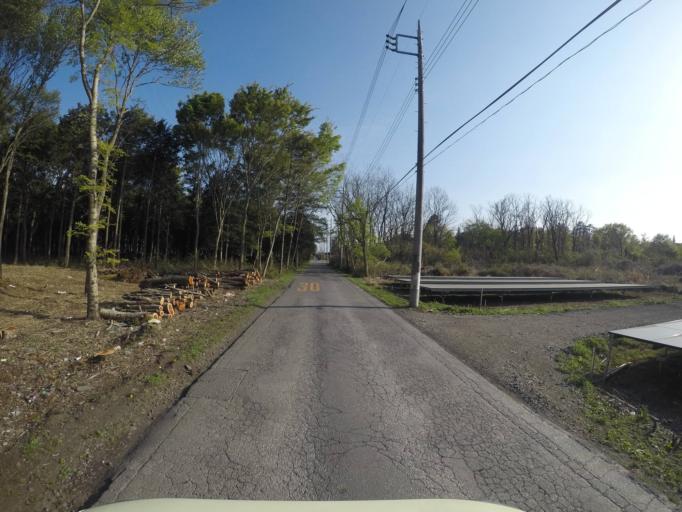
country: JP
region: Ibaraki
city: Ishige
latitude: 36.1580
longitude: 140.0163
